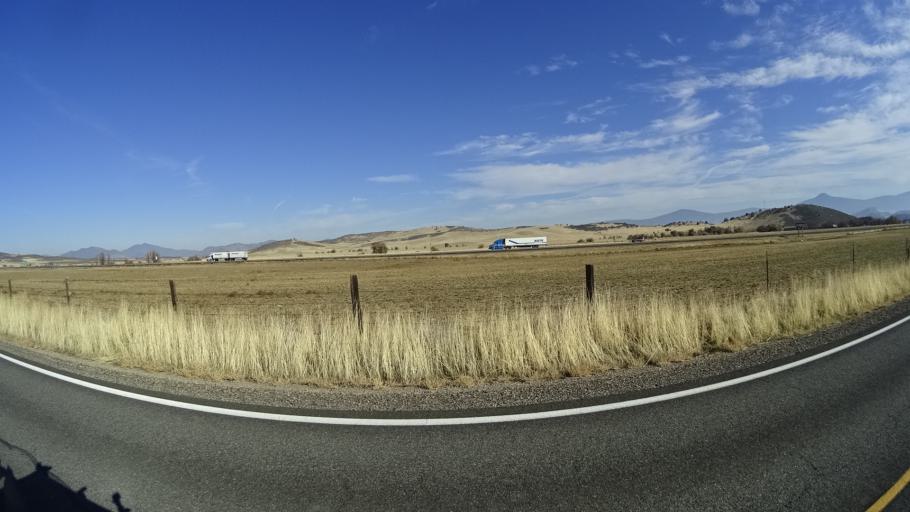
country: US
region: California
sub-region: Siskiyou County
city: Montague
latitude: 41.6487
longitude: -122.5479
